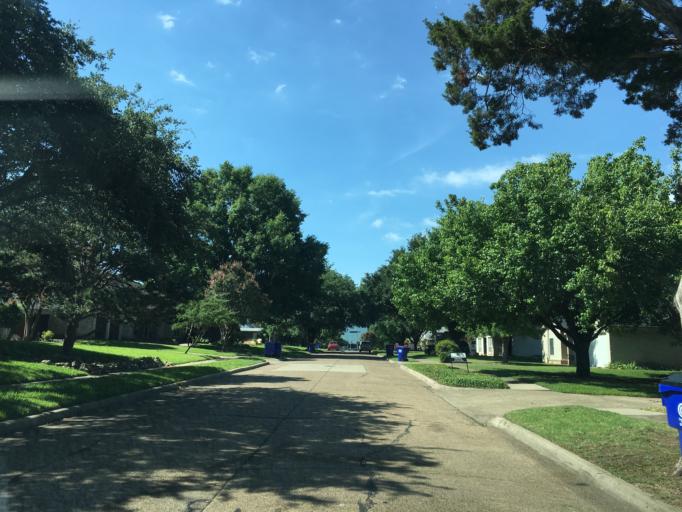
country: US
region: Texas
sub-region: Dallas County
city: Farmers Branch
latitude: 32.9163
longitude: -96.8774
